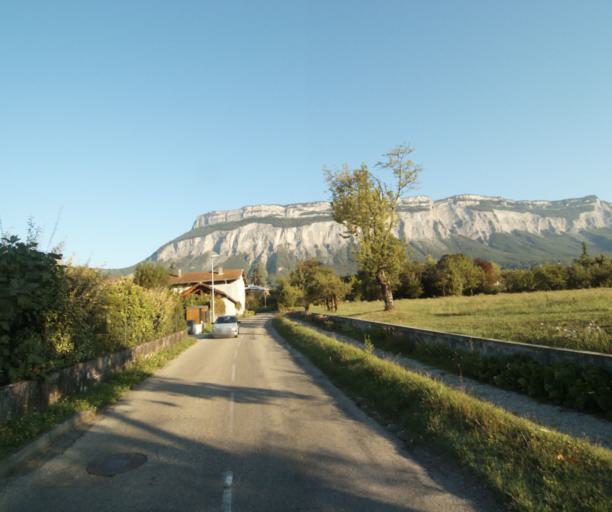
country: FR
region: Rhone-Alpes
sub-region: Departement de l'Isere
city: Montbonnot-Saint-Martin
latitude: 45.2168
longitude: 5.7988
